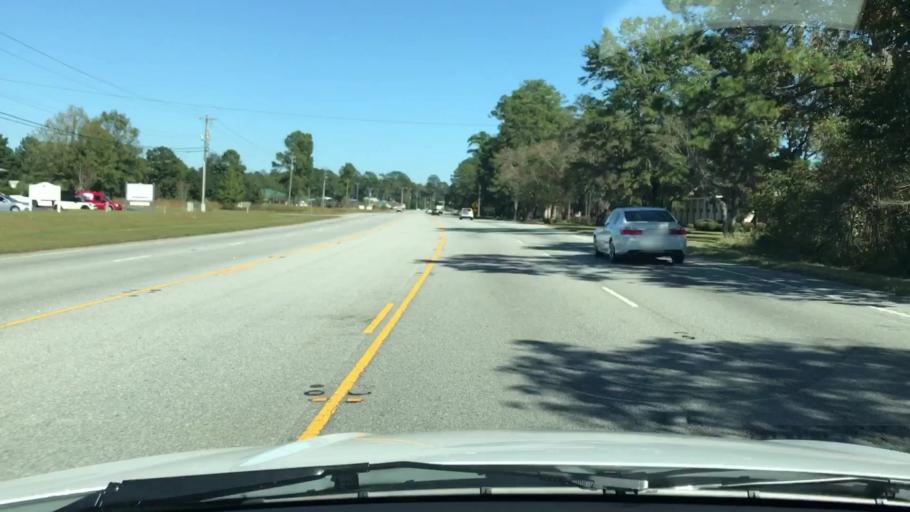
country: US
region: South Carolina
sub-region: Beaufort County
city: Bluffton
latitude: 32.3598
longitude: -80.8736
